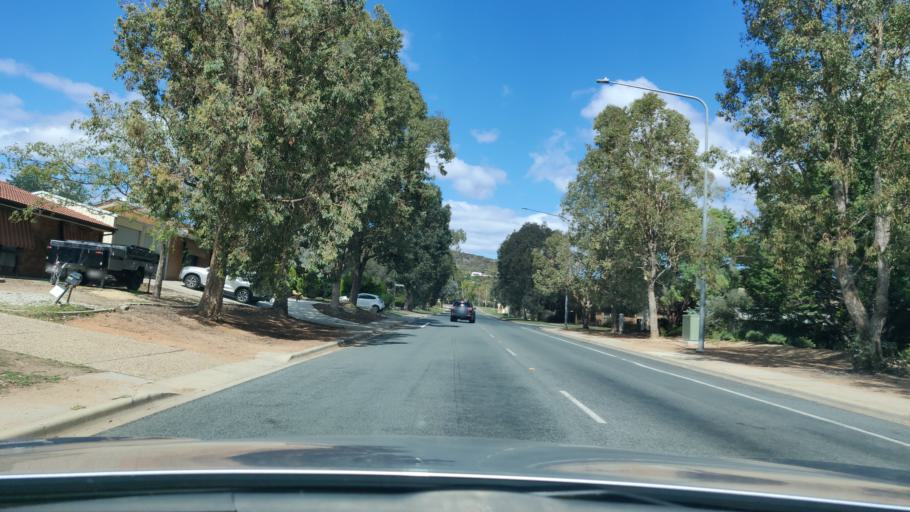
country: AU
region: Australian Capital Territory
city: Macarthur
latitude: -35.4378
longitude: 149.0978
